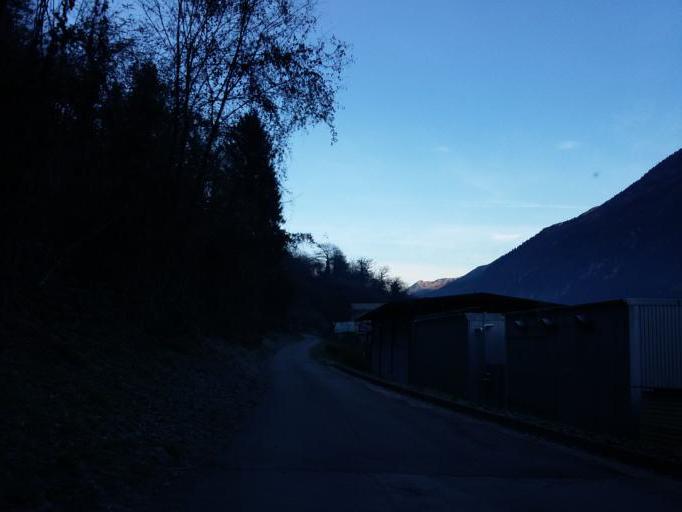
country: IT
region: Trentino-Alto Adige
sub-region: Provincia di Trento
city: Condino
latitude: 45.8805
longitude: 10.5909
